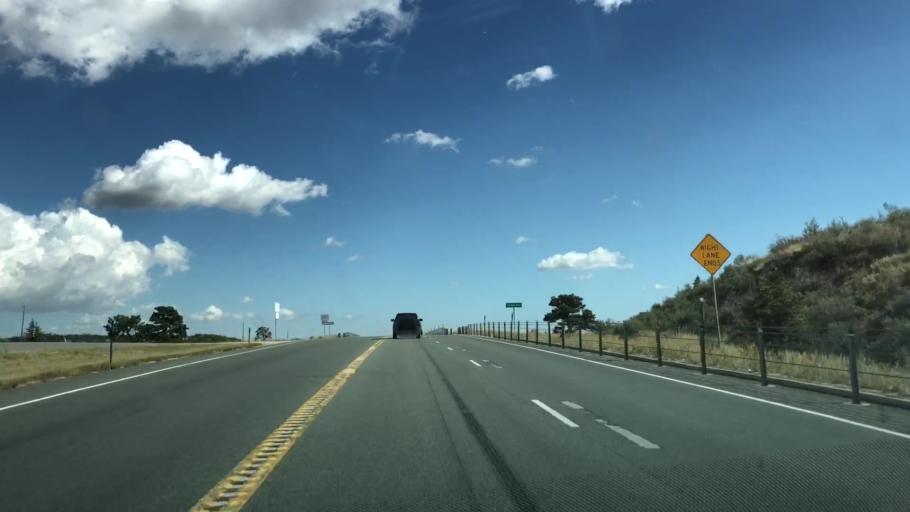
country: US
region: Colorado
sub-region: Larimer County
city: Laporte
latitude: 40.9544
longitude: -105.3504
